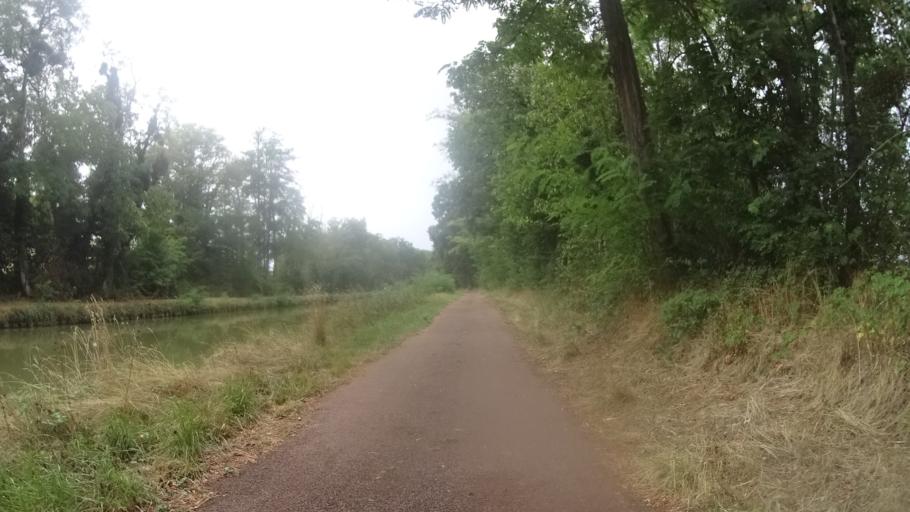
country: FR
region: Bourgogne
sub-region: Departement de la Nievre
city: Imphy
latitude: 46.9114
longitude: 3.2470
